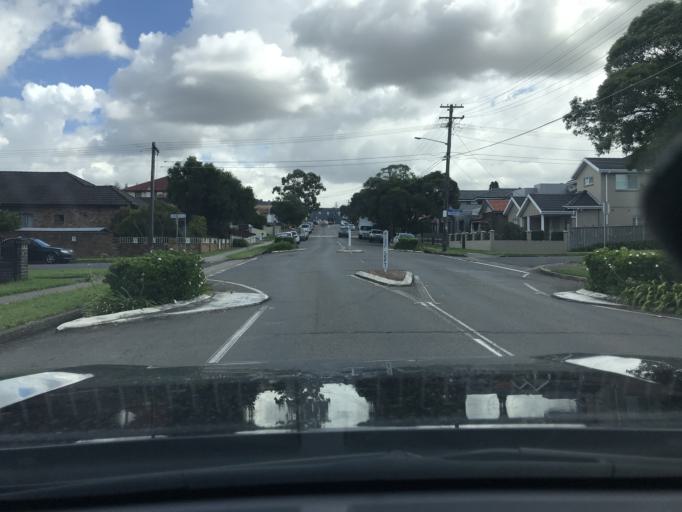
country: AU
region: New South Wales
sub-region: Canada Bay
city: Concord
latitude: -33.8501
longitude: 151.1082
